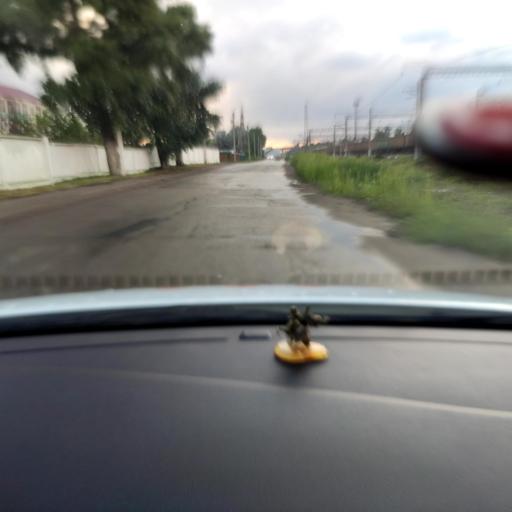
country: RU
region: Tatarstan
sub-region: Zelenodol'skiy Rayon
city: Zelenodolsk
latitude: 55.8414
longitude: 48.5561
